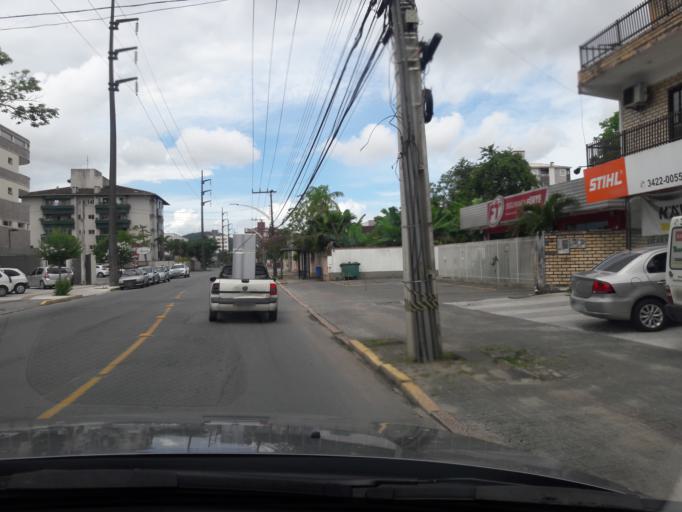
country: BR
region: Santa Catarina
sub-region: Joinville
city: Joinville
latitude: -26.3203
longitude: -48.8517
